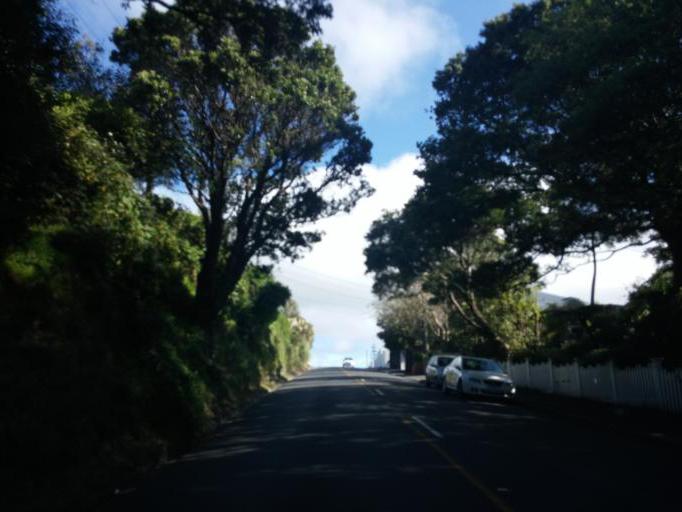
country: NZ
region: Wellington
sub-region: Wellington City
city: Kelburn
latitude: -41.2838
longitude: 174.7497
